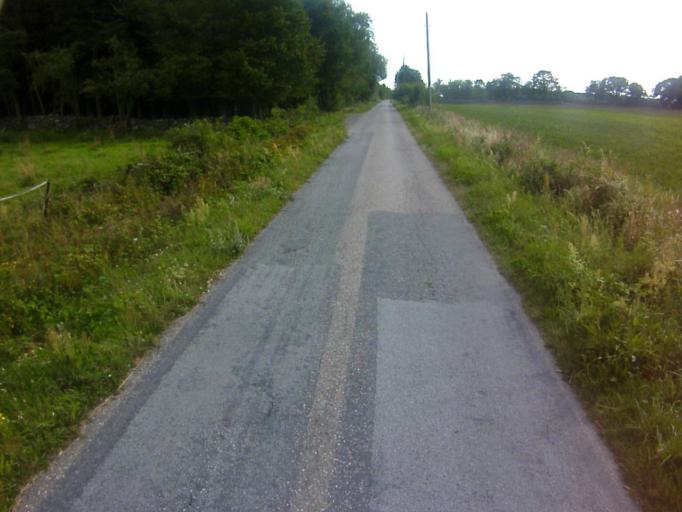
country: SE
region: Blekinge
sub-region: Solvesborgs Kommun
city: Soelvesborg
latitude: 56.0026
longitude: 14.6724
